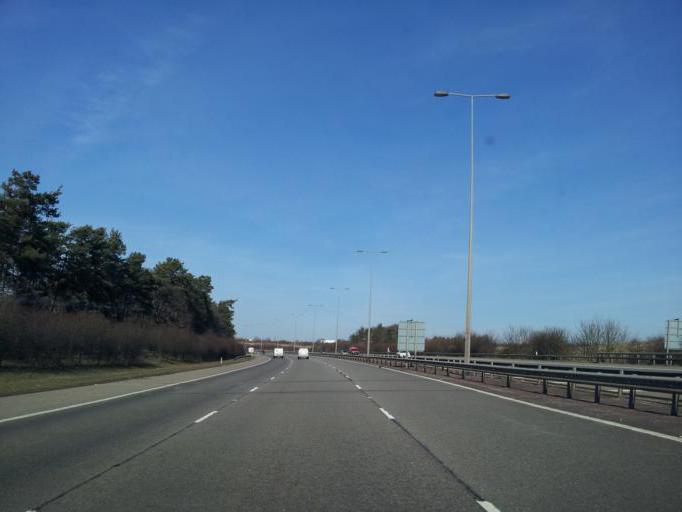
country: GB
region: England
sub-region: Cambridgeshire
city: Great Stukeley
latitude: 52.3701
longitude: -0.2532
